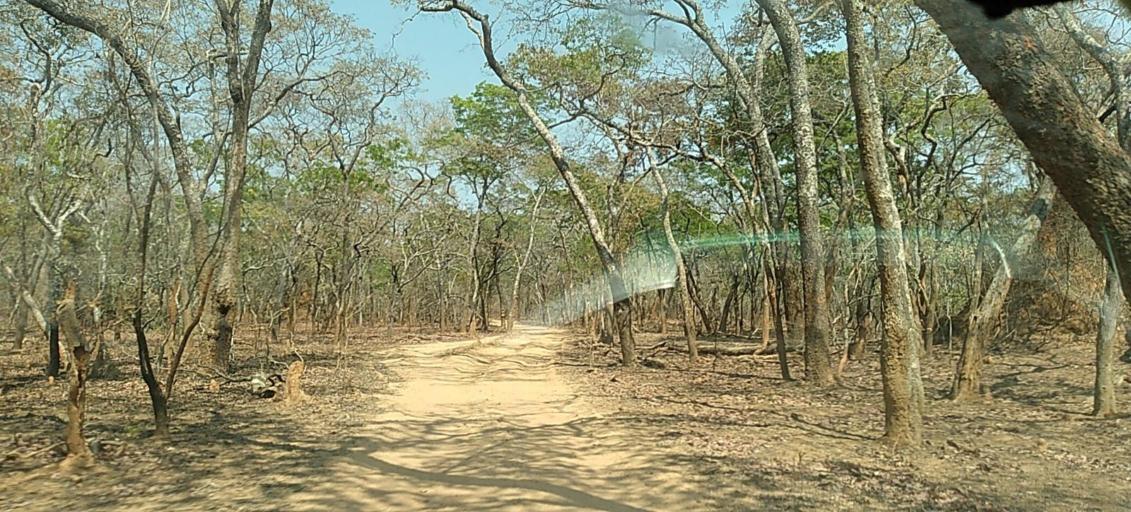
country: ZM
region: North-Western
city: Kasempa
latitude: -13.3925
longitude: 25.6160
